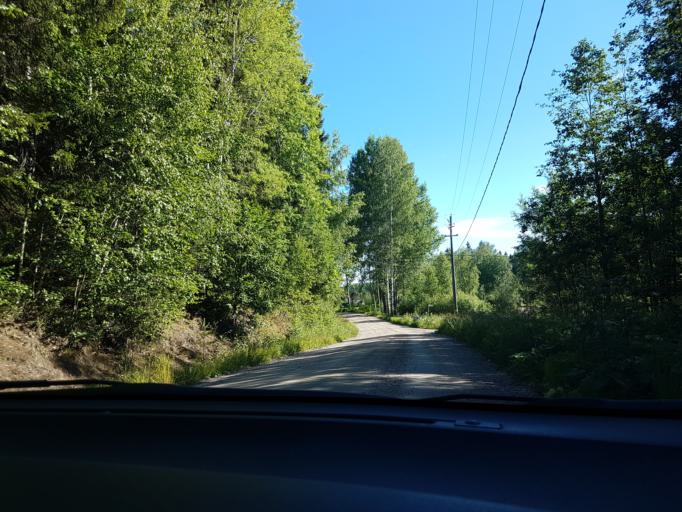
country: FI
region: Uusimaa
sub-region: Helsinki
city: Sibbo
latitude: 60.2845
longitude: 25.2395
